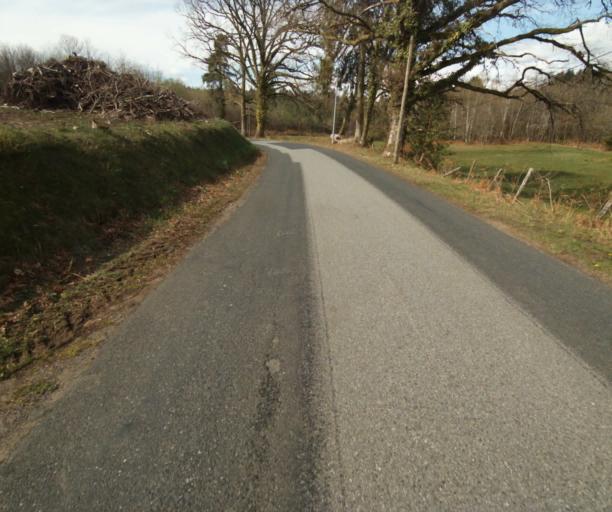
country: FR
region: Limousin
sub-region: Departement de la Correze
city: Correze
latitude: 45.3509
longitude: 1.9037
